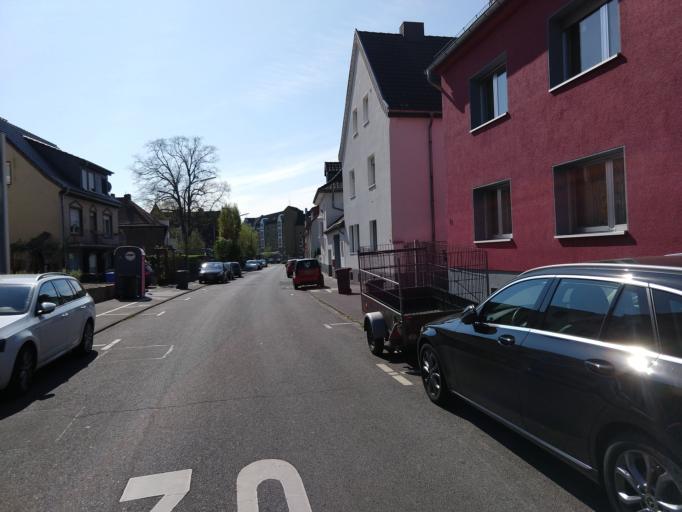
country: DE
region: North Rhine-Westphalia
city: Wesseling
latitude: 50.8261
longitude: 6.9794
